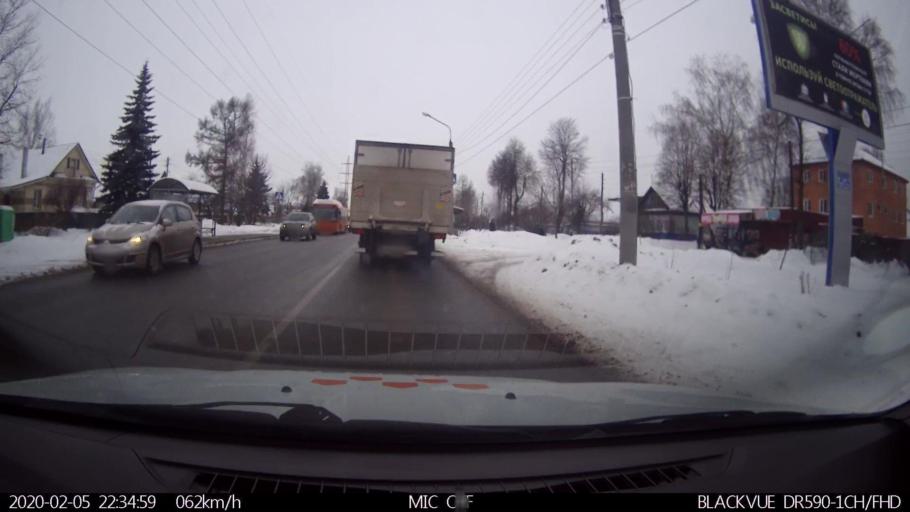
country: RU
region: Nizjnij Novgorod
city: Imeni Stepana Razina
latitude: 54.7350
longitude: 44.2331
